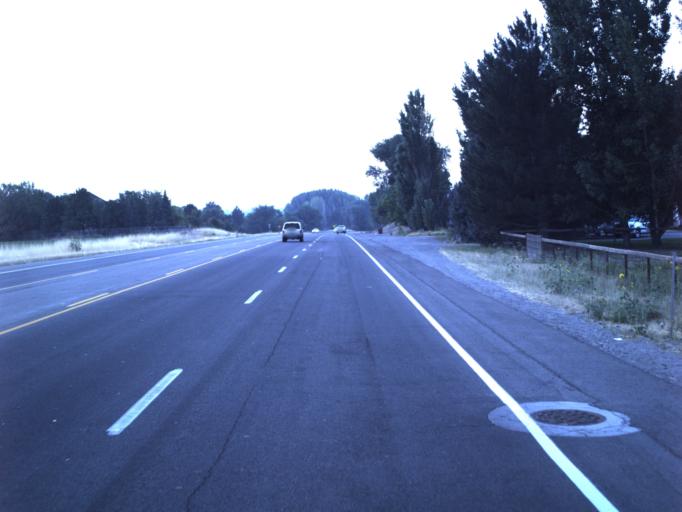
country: US
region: Utah
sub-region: Utah County
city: Mapleton
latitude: 40.1420
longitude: -111.6006
